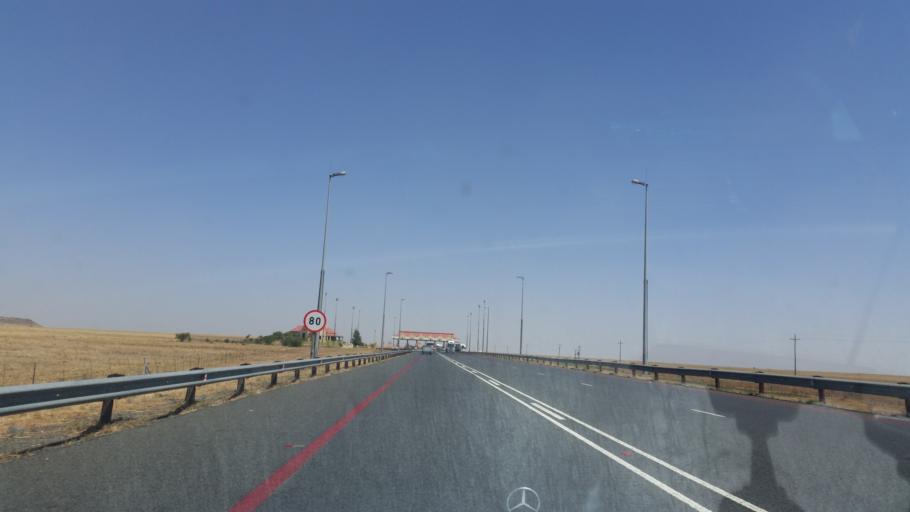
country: ZA
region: Orange Free State
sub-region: Lejweleputswa District Municipality
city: Brandfort
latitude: -28.7962
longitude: 26.6938
